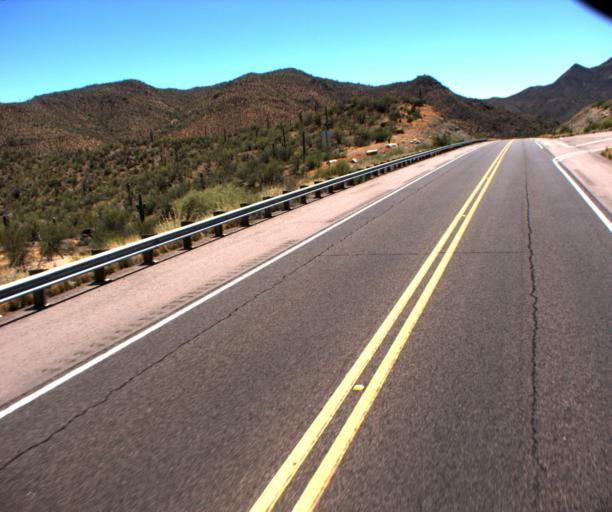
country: US
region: Arizona
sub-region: Pinal County
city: Kearny
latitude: 33.0827
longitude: -110.7170
